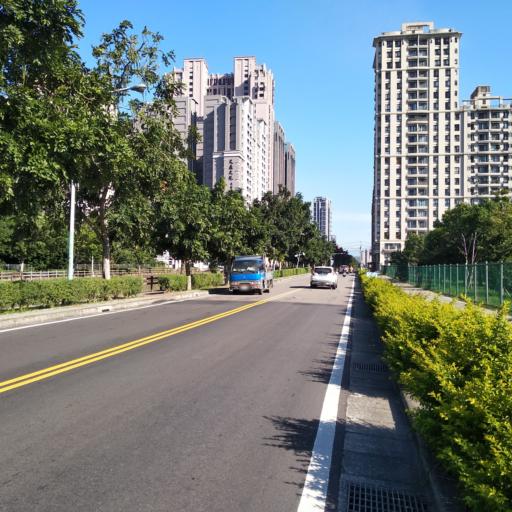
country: TW
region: Taiwan
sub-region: Hsinchu
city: Zhubei
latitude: 24.8270
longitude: 121.0236
